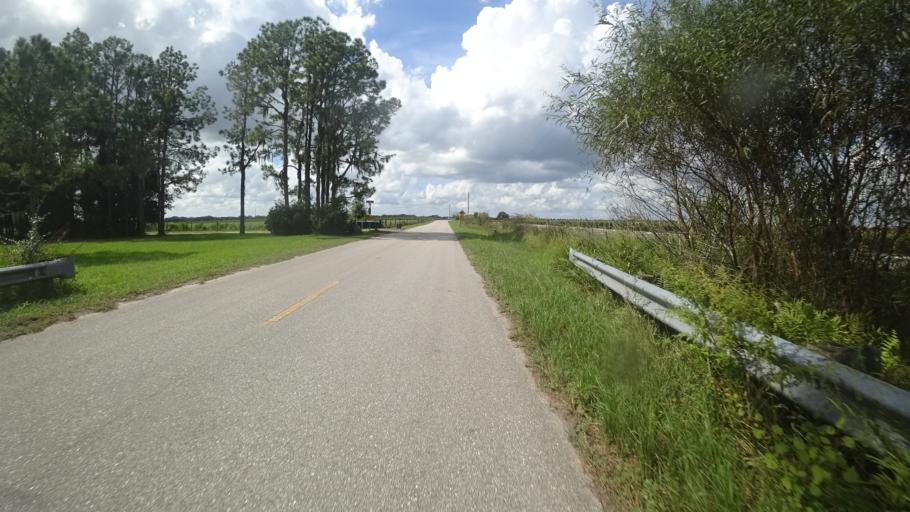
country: US
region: Florida
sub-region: Hillsborough County
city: Wimauma
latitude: 27.6119
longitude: -82.2287
